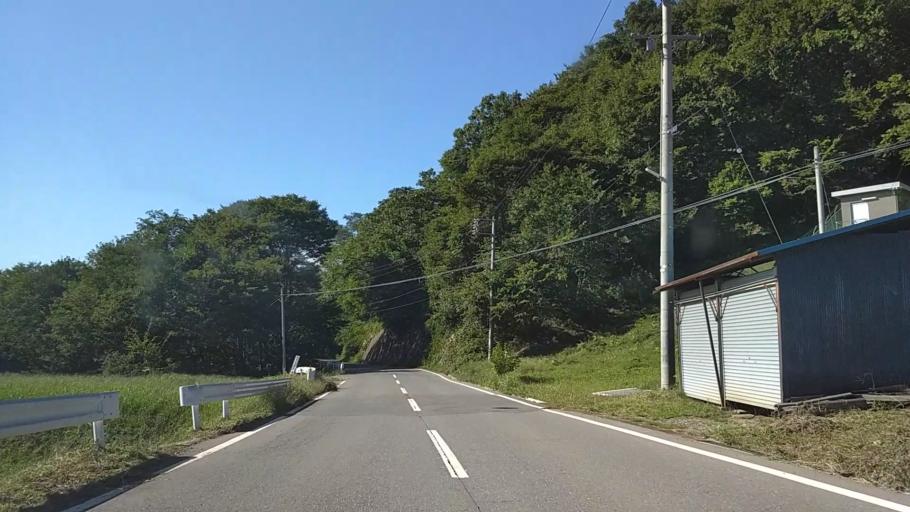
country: JP
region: Nagano
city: Nagano-shi
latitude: 36.6061
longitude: 138.0923
